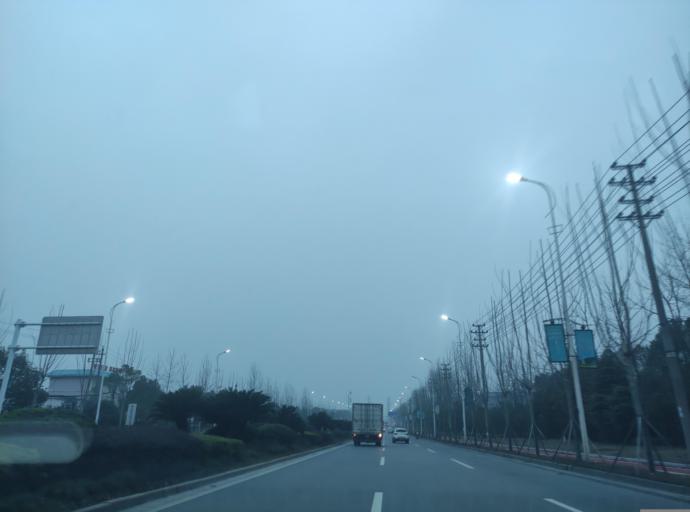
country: CN
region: Jiangxi Sheng
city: Pingxiang
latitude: 27.6661
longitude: 113.8750
